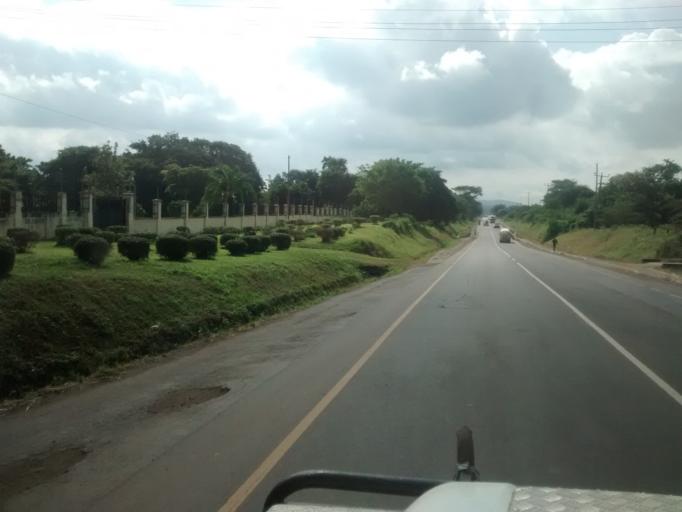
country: TZ
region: Arusha
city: Usa River
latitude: -3.3744
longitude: 36.8396
